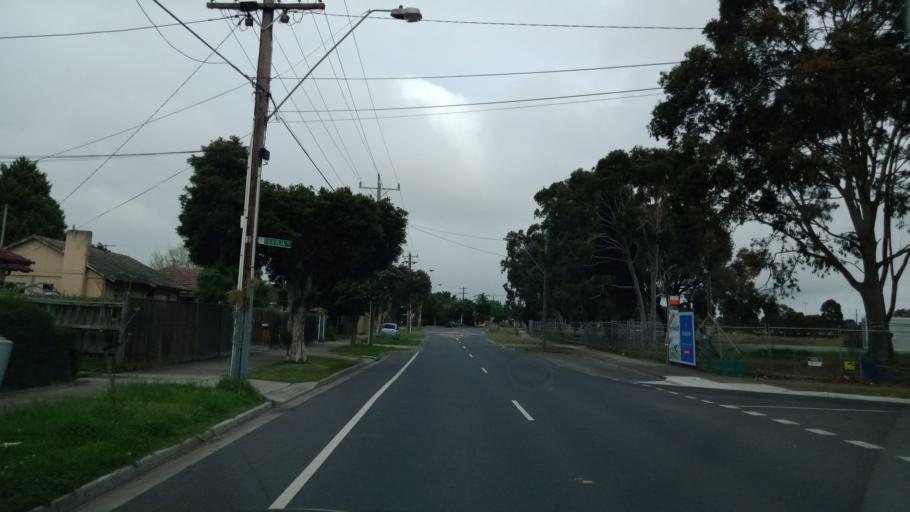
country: AU
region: Victoria
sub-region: Casey
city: Doveton
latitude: -37.9962
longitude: 145.2314
